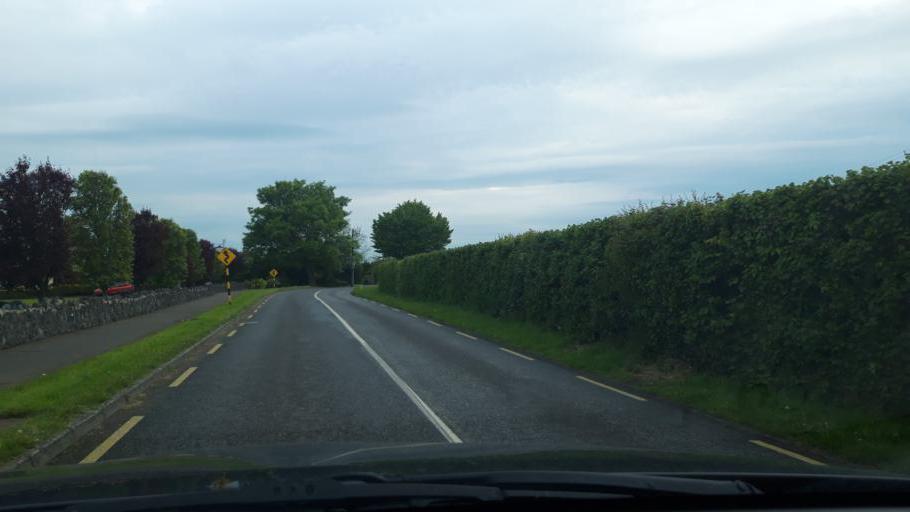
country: IE
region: Leinster
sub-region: Kildare
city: Celbridge
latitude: 53.2986
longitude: -6.5670
